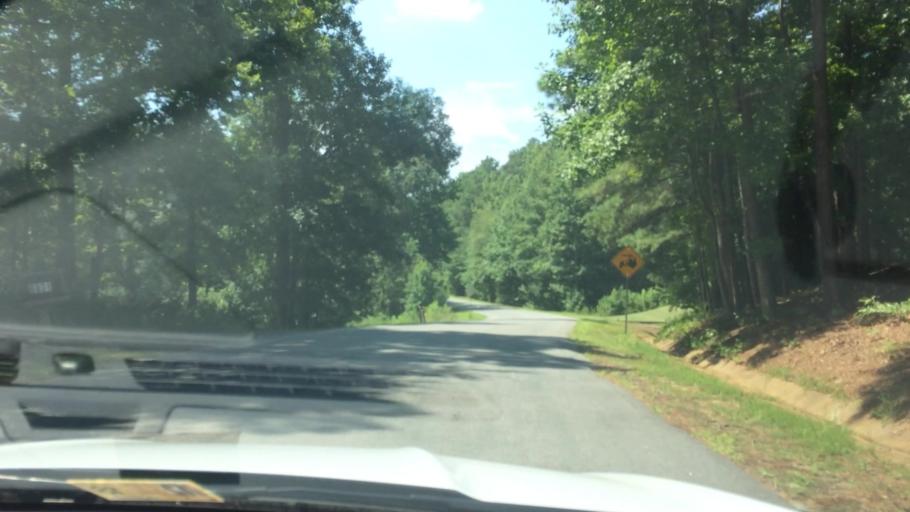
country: US
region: Virginia
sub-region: Henrico County
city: Sandston
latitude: 37.5000
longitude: -77.1711
